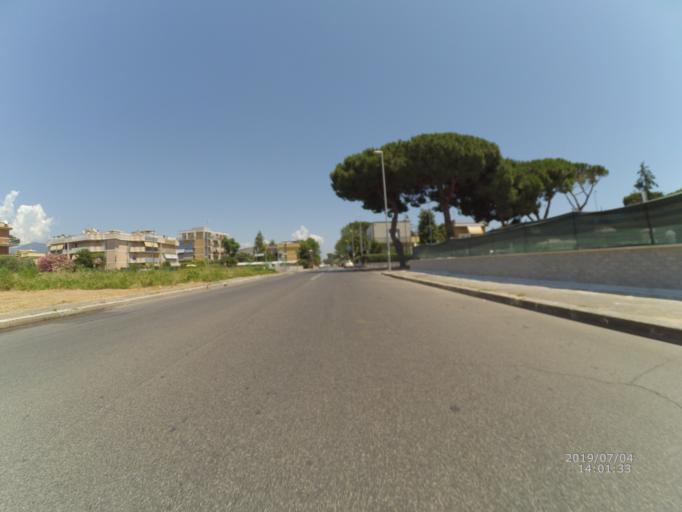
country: IT
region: Latium
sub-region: Provincia di Latina
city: Terracina
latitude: 41.2862
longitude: 13.2270
